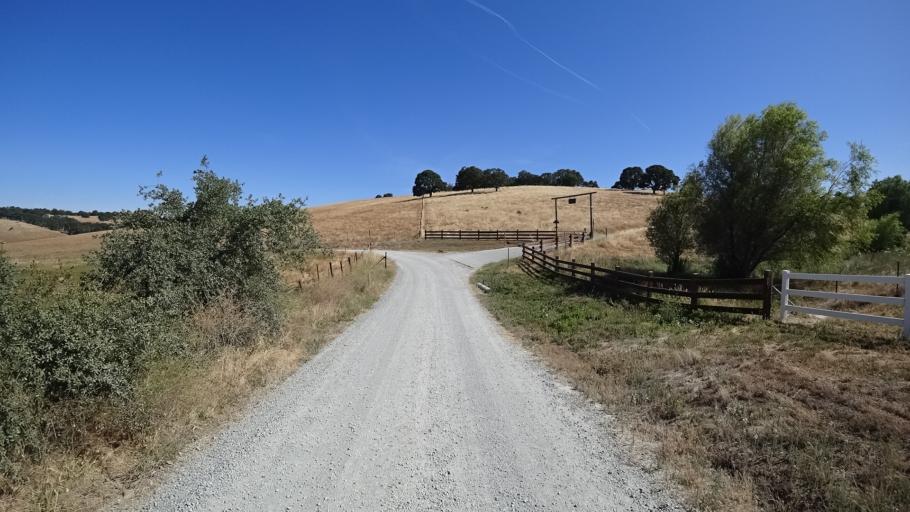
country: US
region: California
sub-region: Amador County
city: Jackson
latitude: 38.2626
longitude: -120.7698
